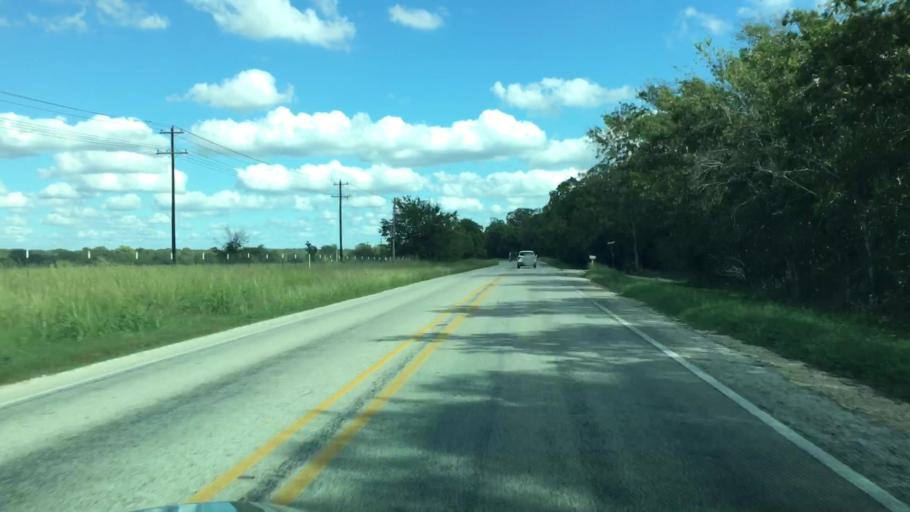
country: US
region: Texas
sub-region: Blanco County
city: Blanco
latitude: 30.0916
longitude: -98.3883
